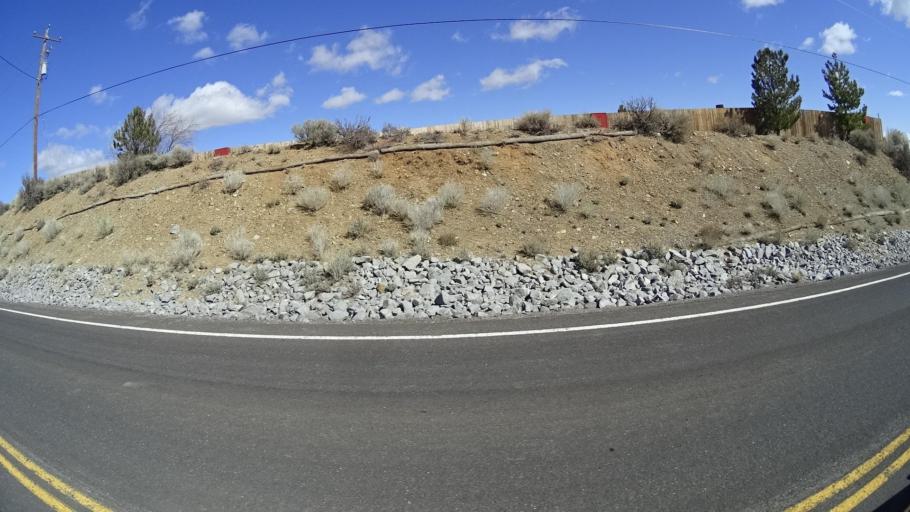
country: US
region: Nevada
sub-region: Washoe County
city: Lemmon Valley
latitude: 39.6174
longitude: -119.8863
